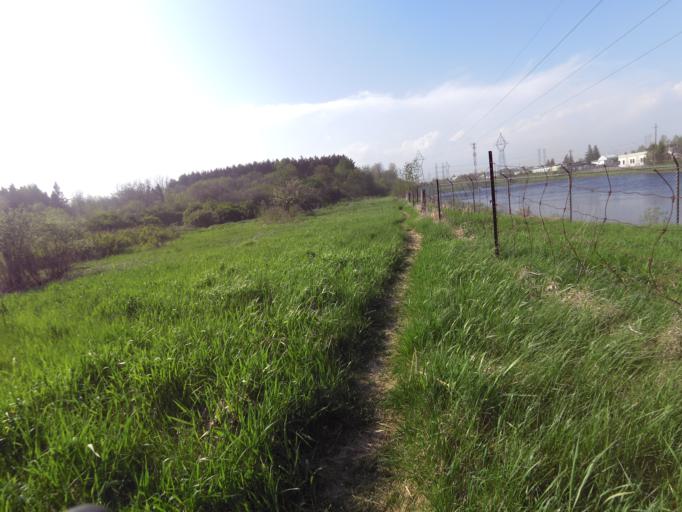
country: CA
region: Ontario
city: Ottawa
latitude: 45.3293
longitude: -75.7289
